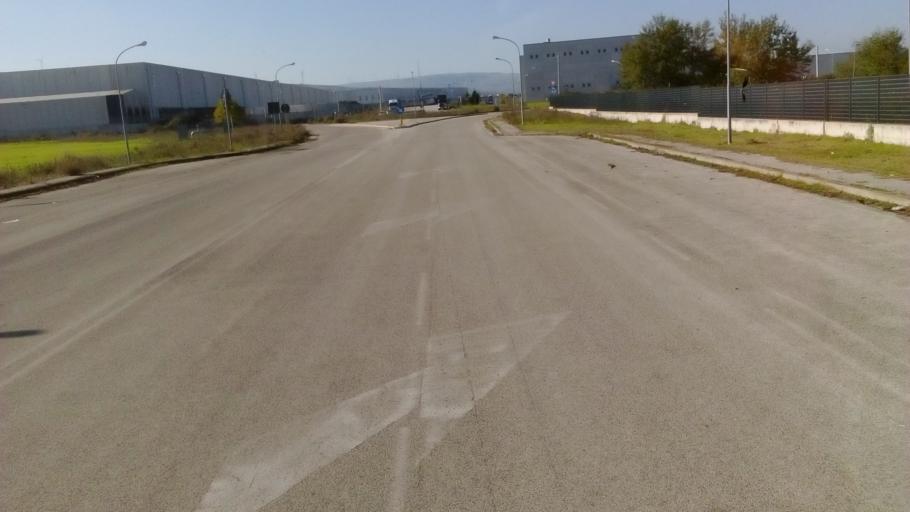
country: IT
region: Basilicate
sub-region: Provincia di Potenza
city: Melfi
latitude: 41.0782
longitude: 15.6611
